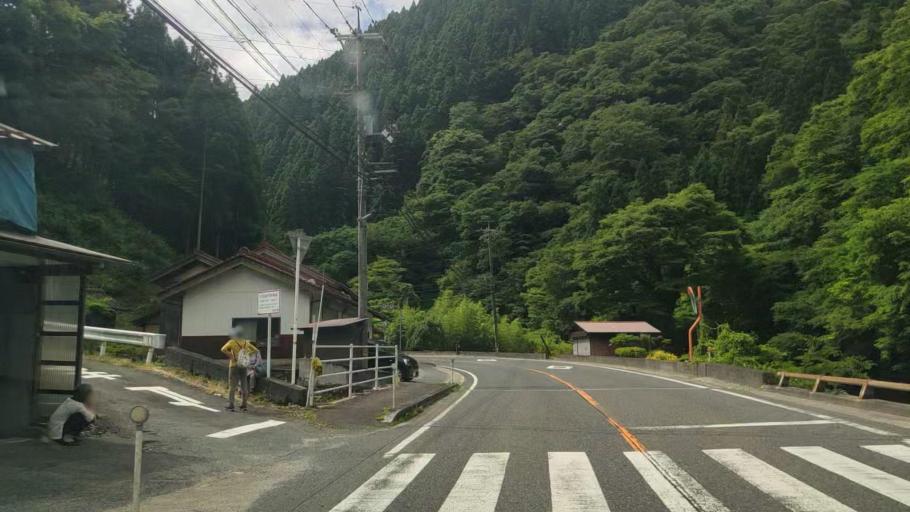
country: JP
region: Tottori
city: Yonago
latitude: 35.2234
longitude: 133.4480
